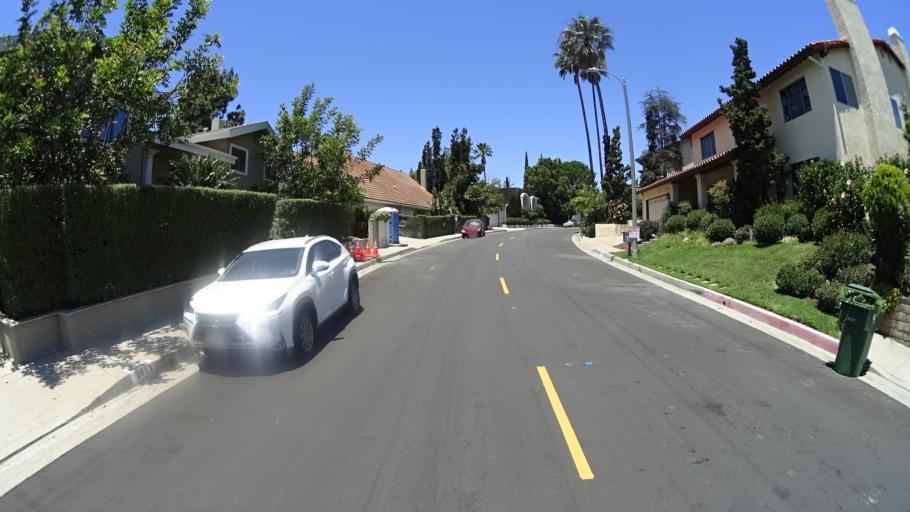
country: US
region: California
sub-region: Los Angeles County
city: West Hollywood
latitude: 34.1148
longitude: -118.3686
